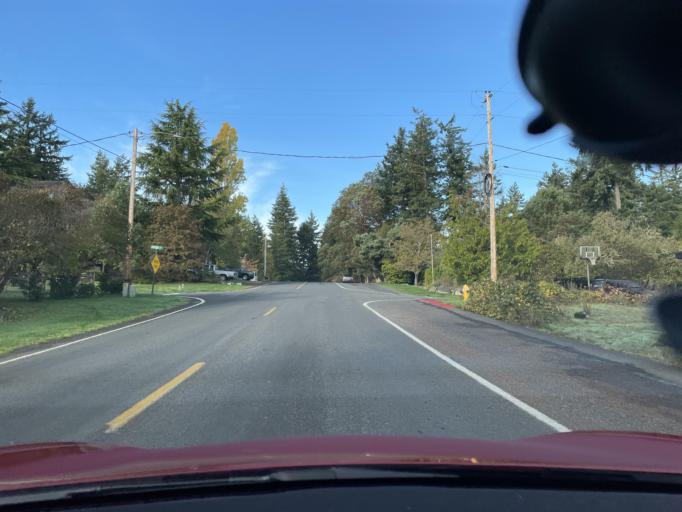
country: US
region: Washington
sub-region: San Juan County
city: Friday Harbor
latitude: 48.5345
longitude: -123.0277
